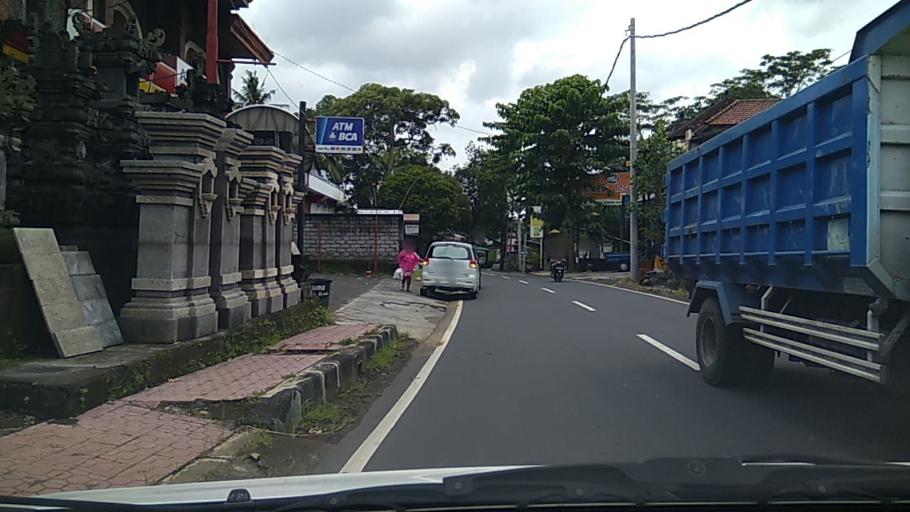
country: ID
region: Bali
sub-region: Kabupaten Gianyar
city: Ubud
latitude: -8.5233
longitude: 115.2894
